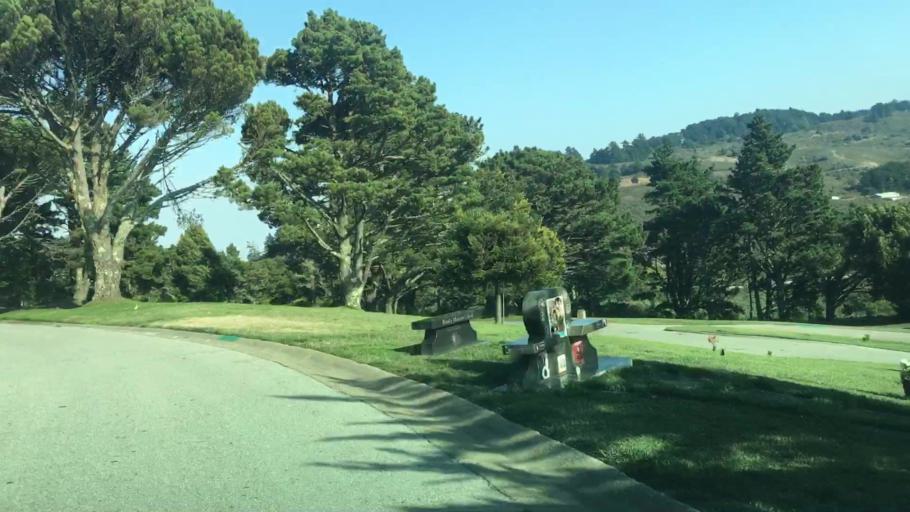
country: US
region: California
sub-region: San Mateo County
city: Highlands-Baywood Park
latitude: 37.4956
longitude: -122.3738
